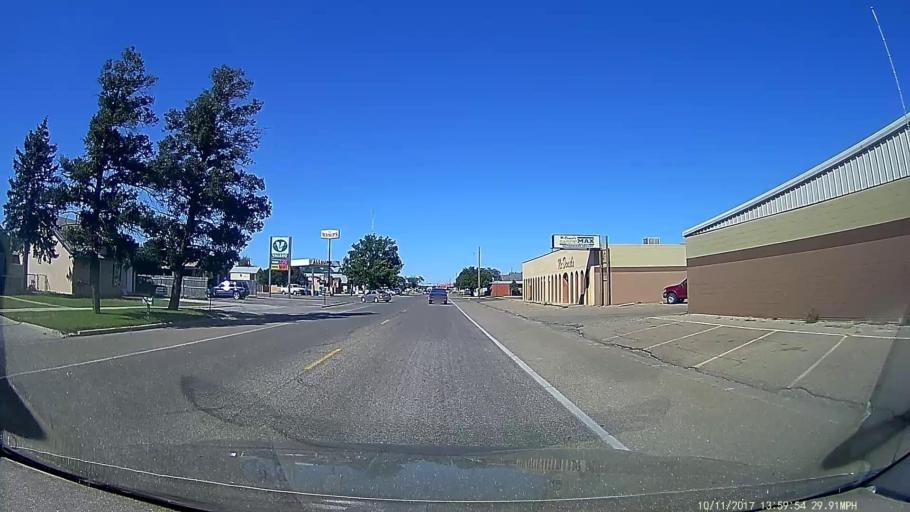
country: US
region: New Mexico
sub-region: Curry County
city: Clovis
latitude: 34.4082
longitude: -103.2066
